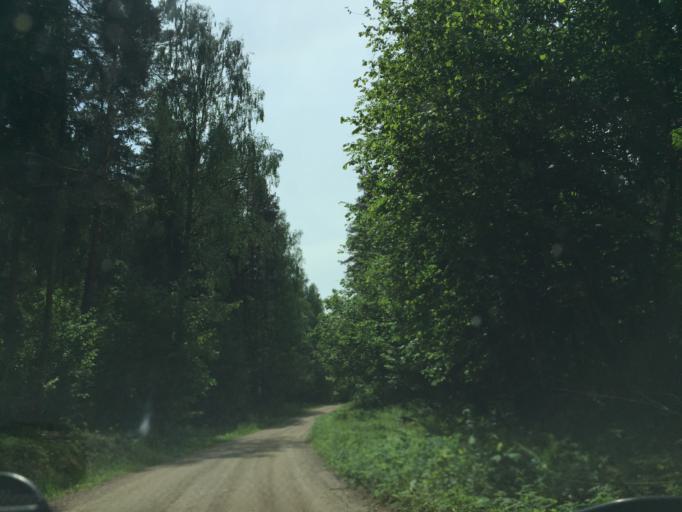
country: LV
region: Koceni
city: Koceni
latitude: 57.4576
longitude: 25.2709
